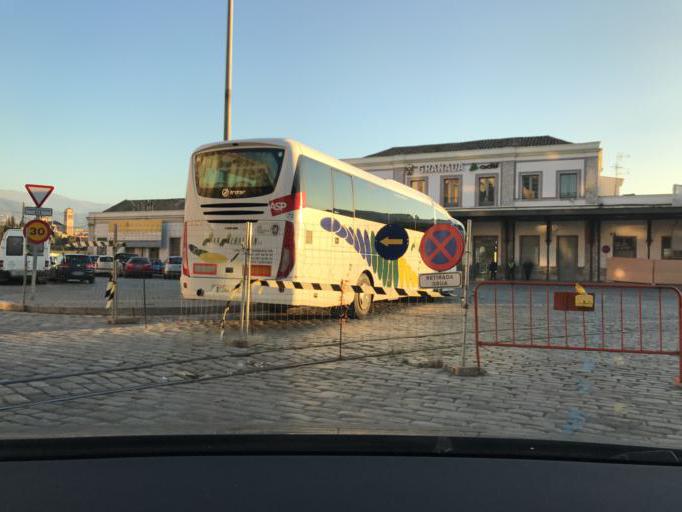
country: ES
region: Andalusia
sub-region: Provincia de Granada
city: Granada
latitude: 37.1847
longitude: -3.6091
